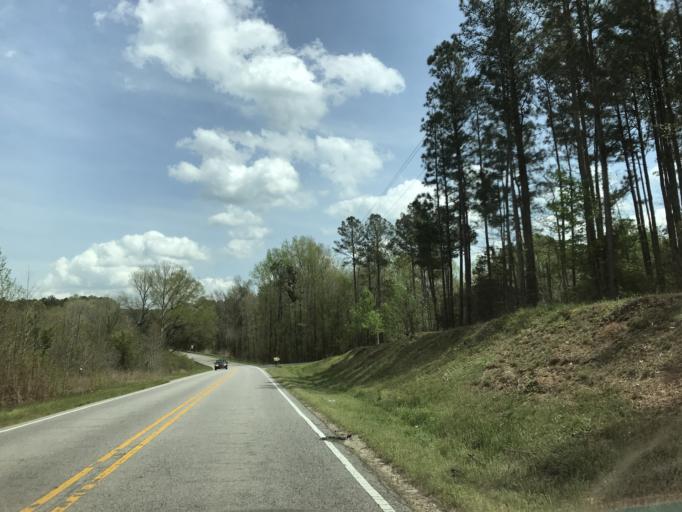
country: US
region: North Carolina
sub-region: Nash County
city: Spring Hope
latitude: 35.9662
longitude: -78.2236
